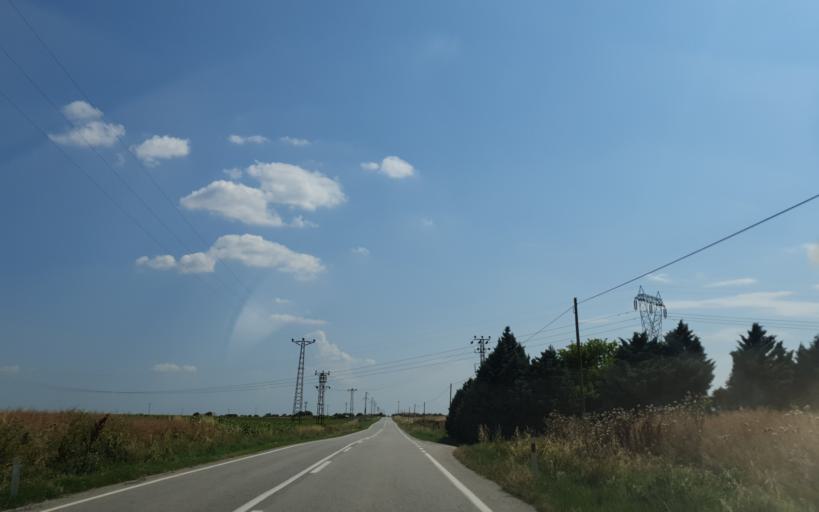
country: TR
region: Kirklareli
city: Buyukkaristiran
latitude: 41.3445
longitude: 27.5471
